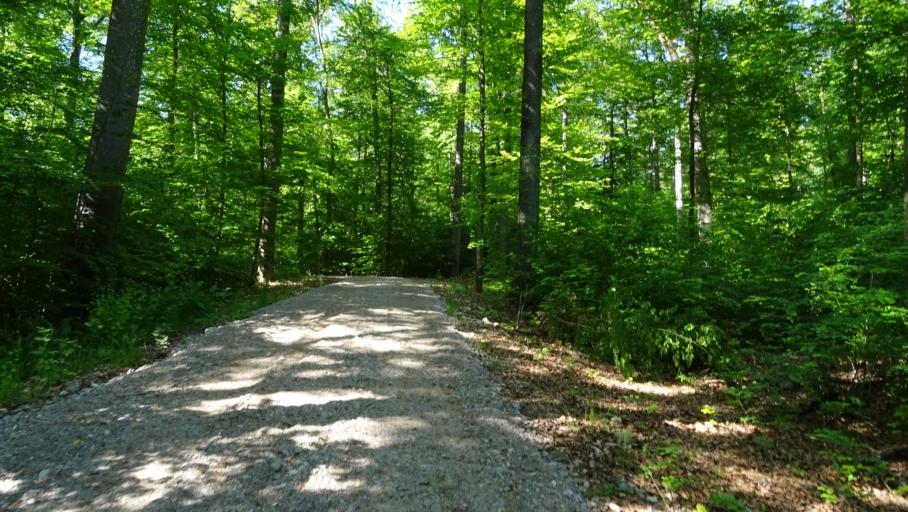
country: DE
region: Baden-Wuerttemberg
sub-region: Karlsruhe Region
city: Obrigheim
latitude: 49.3710
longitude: 9.1048
